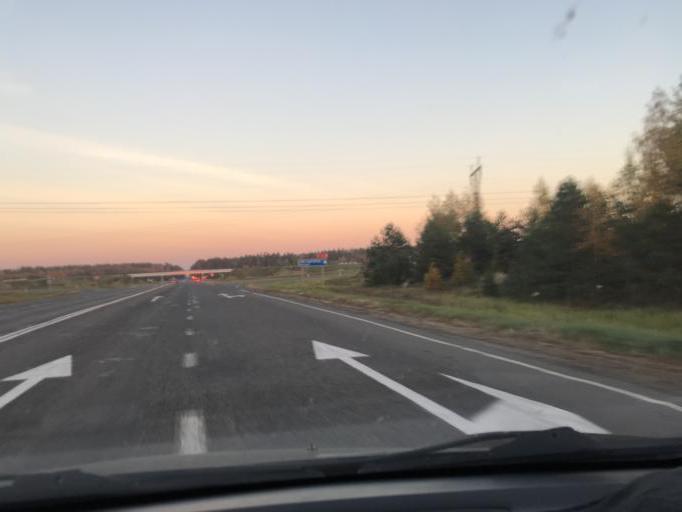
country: BY
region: Mogilev
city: Babruysk
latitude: 53.1046
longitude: 29.0510
